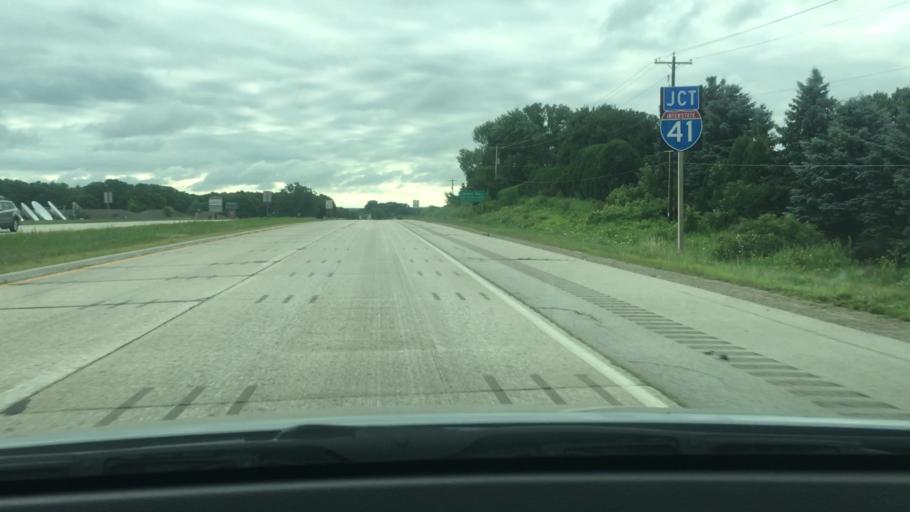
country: US
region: Wisconsin
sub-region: Brown County
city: Ashwaubenon
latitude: 44.4908
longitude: -88.0940
